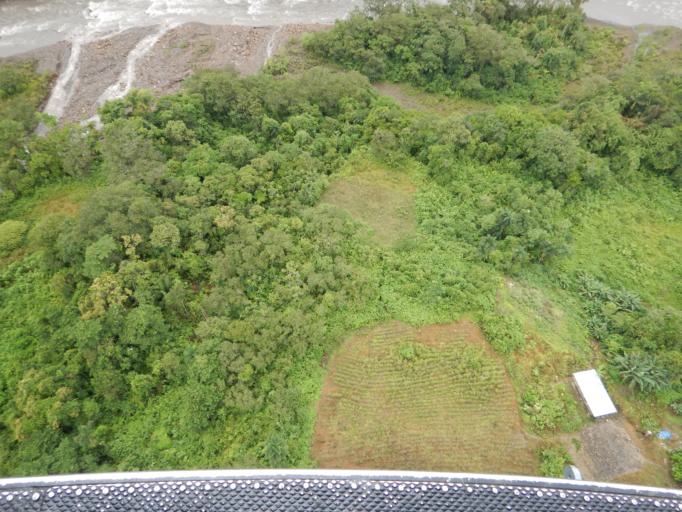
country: BO
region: Cochabamba
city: Totora
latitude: -17.3366
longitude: -65.2298
